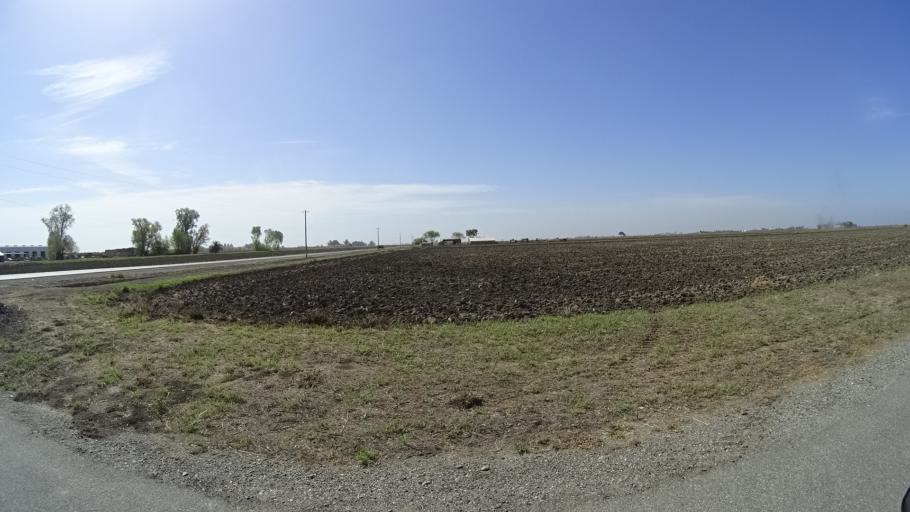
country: US
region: California
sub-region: Glenn County
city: Hamilton City
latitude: 39.6162
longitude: -122.0655
